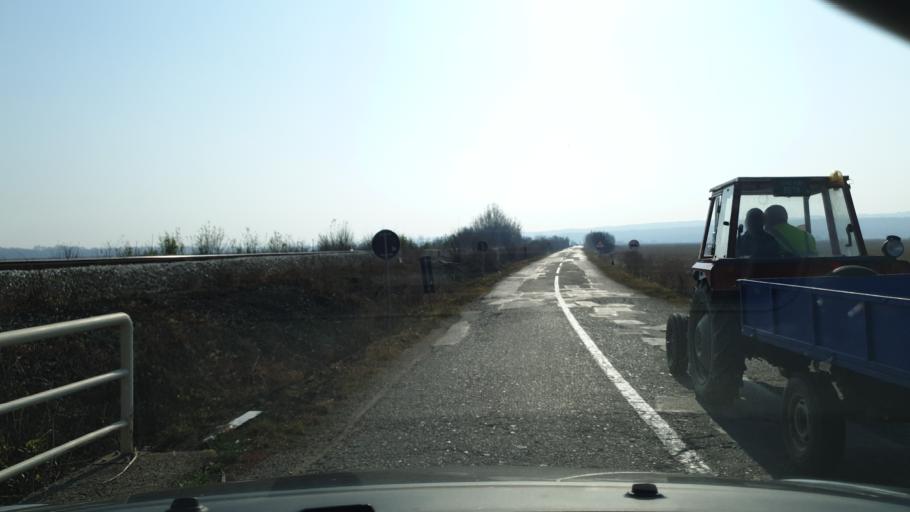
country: BG
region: Vidin
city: Bregovo
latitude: 44.1874
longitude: 22.5950
